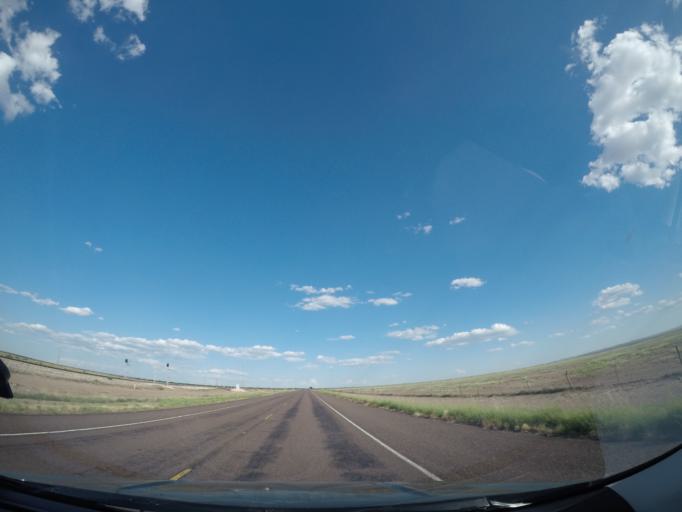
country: US
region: Texas
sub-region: Presidio County
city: Marfa
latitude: 30.4192
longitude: -104.2856
